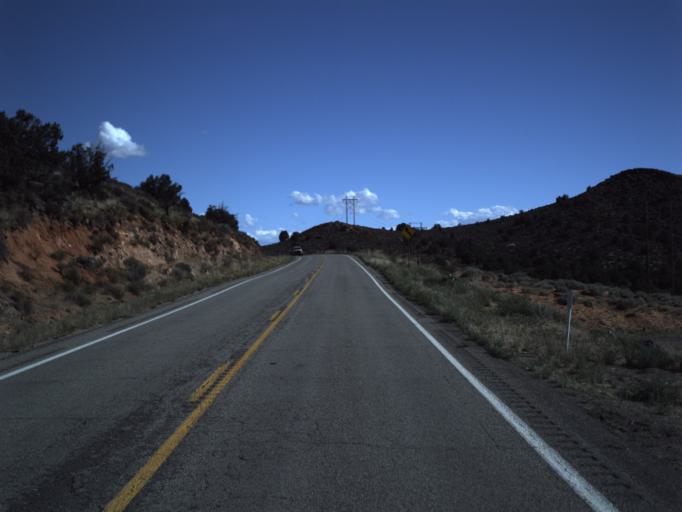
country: US
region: Utah
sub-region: Washington County
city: Toquerville
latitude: 37.2790
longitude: -113.3040
